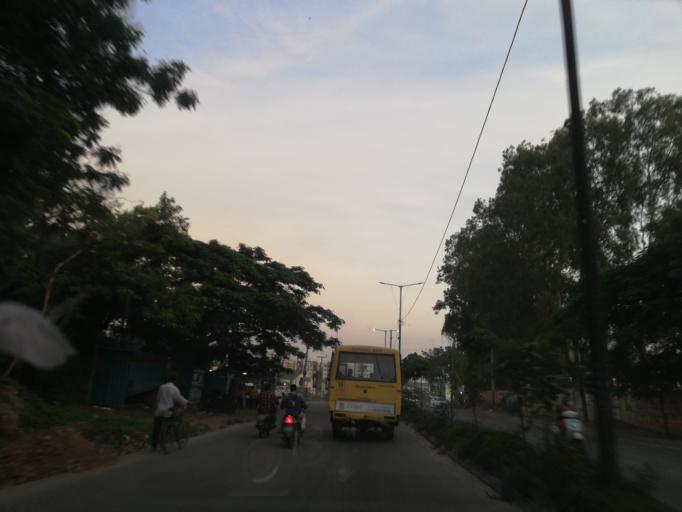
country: IN
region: Telangana
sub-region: Rangareddi
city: Kukatpalli
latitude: 17.5104
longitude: 78.3618
